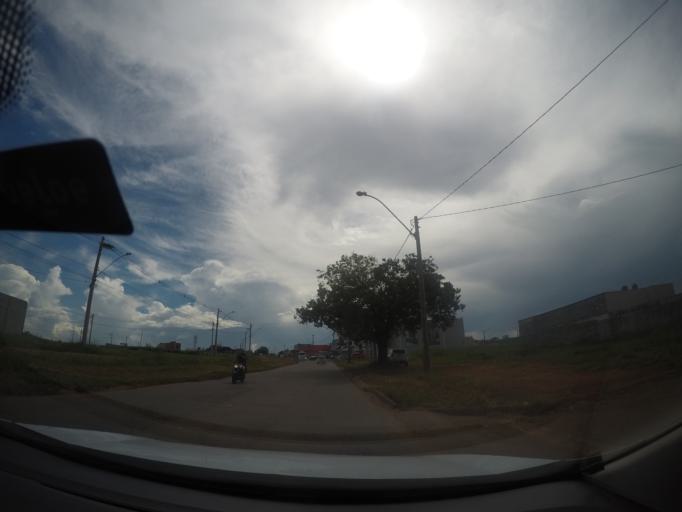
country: BR
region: Goias
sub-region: Goiania
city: Goiania
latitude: -16.6848
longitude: -49.3672
